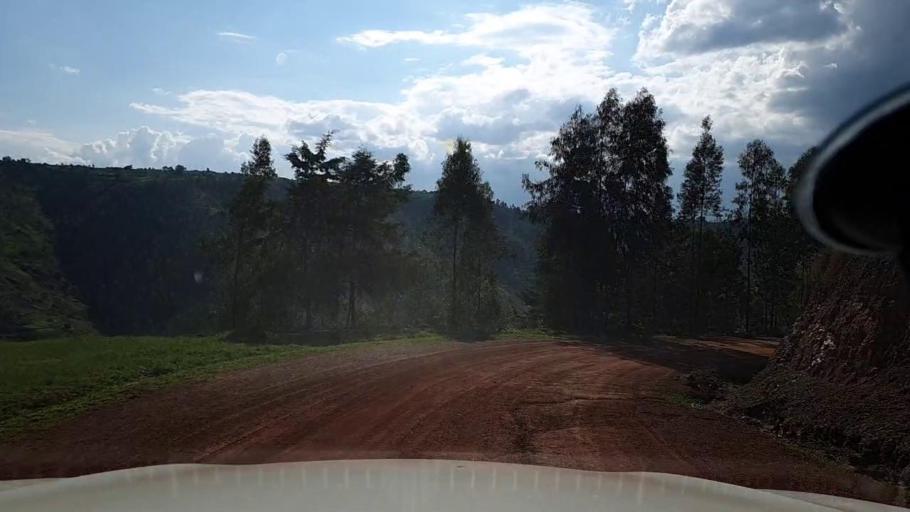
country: RW
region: Kigali
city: Kigali
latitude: -1.8450
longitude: 29.8613
